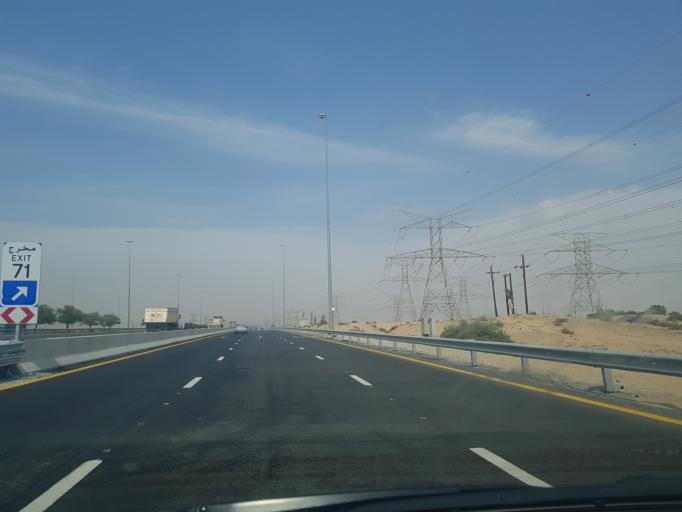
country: AE
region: Ash Shariqah
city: Sharjah
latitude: 25.2204
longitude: 55.5582
